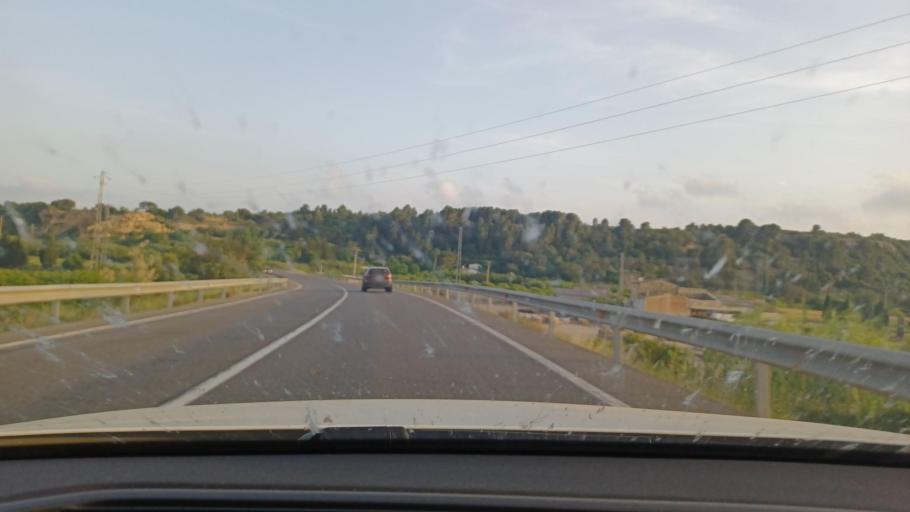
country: ES
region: Catalonia
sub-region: Provincia de Tarragona
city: Tortosa
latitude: 40.7908
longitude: 0.4960
